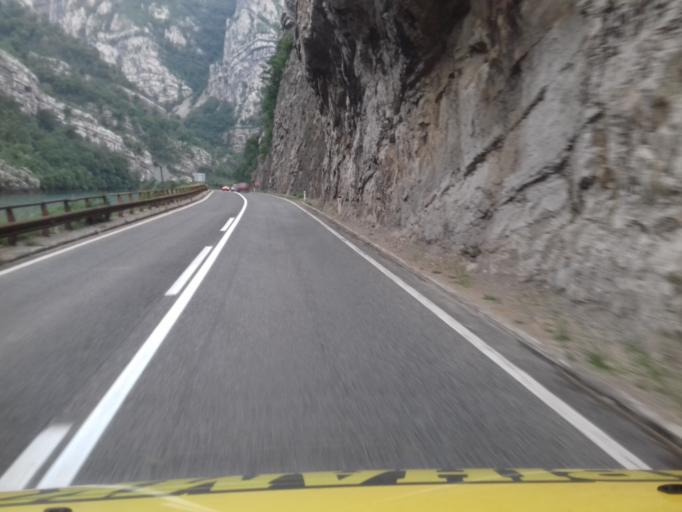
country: BA
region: Federation of Bosnia and Herzegovina
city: Jablanica
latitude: 43.6103
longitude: 17.7402
